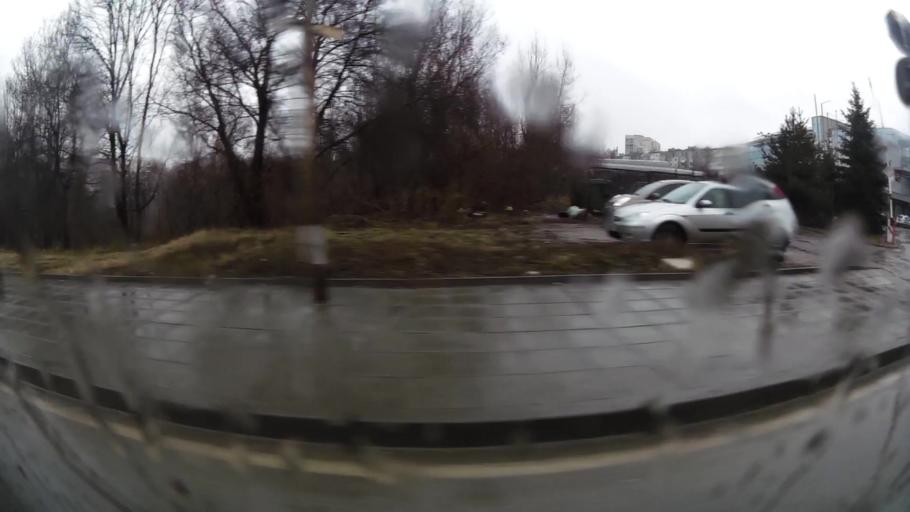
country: BG
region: Sofia-Capital
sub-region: Stolichna Obshtina
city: Sofia
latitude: 42.6499
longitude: 23.3665
